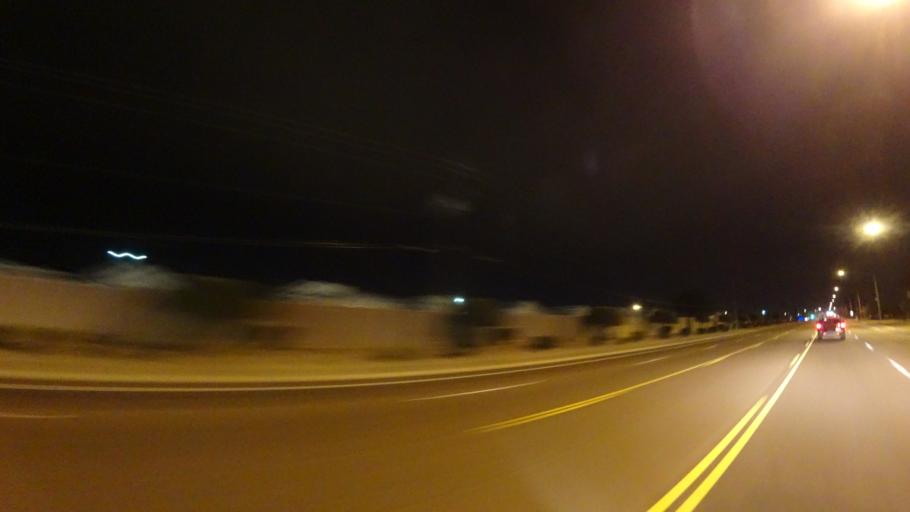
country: US
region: Arizona
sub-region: Maricopa County
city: Mesa
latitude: 33.4221
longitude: -111.7365
